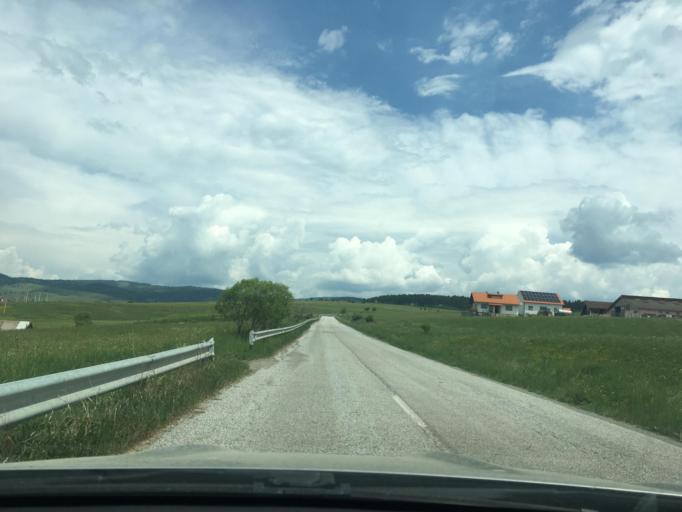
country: RO
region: Harghita
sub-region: Comuna Ditrau
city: Ditrau
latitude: 46.8438
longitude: 25.4997
